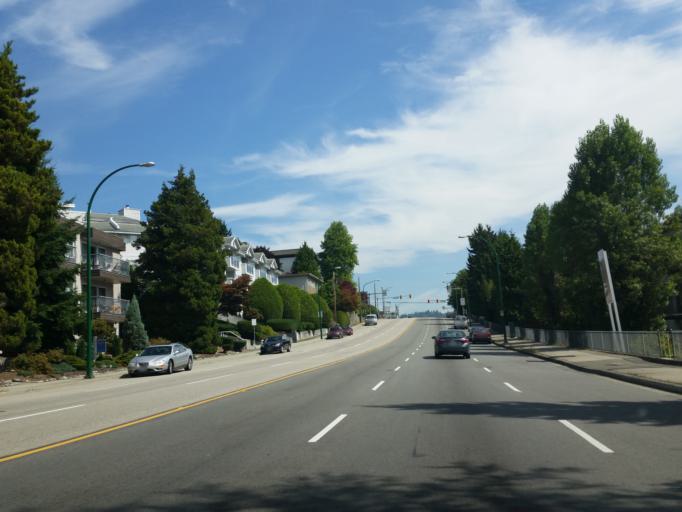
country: CA
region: British Columbia
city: Burnaby
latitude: 49.2803
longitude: -122.9872
